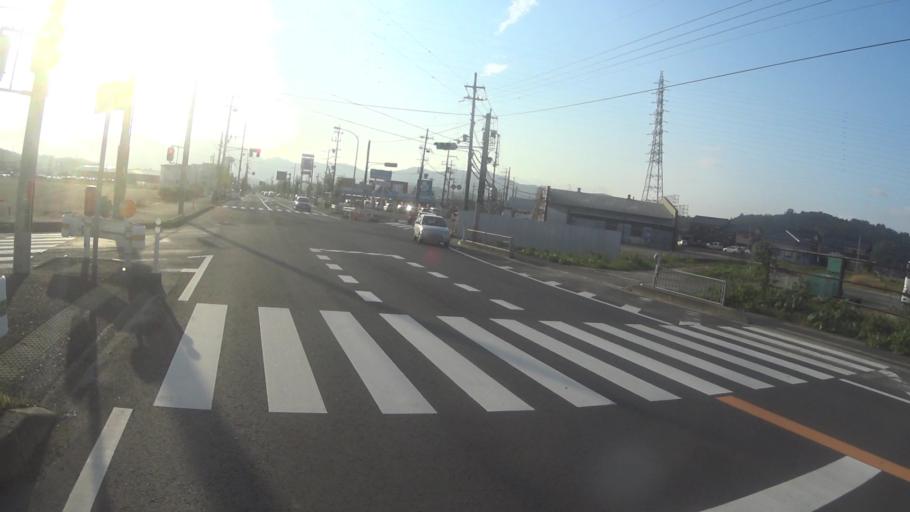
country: JP
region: Kyoto
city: Miyazu
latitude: 35.6096
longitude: 135.0711
